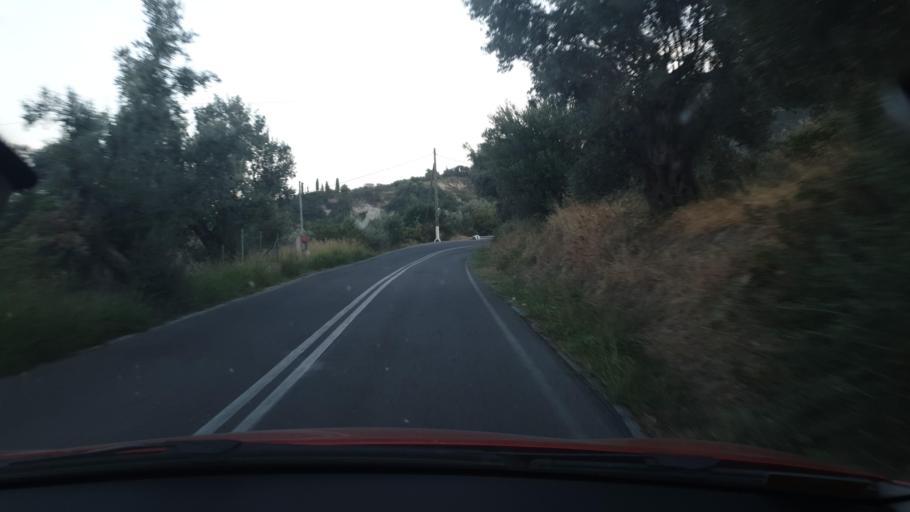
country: GR
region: Central Greece
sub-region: Nomos Evvoias
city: Kymi
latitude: 38.6314
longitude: 24.1163
